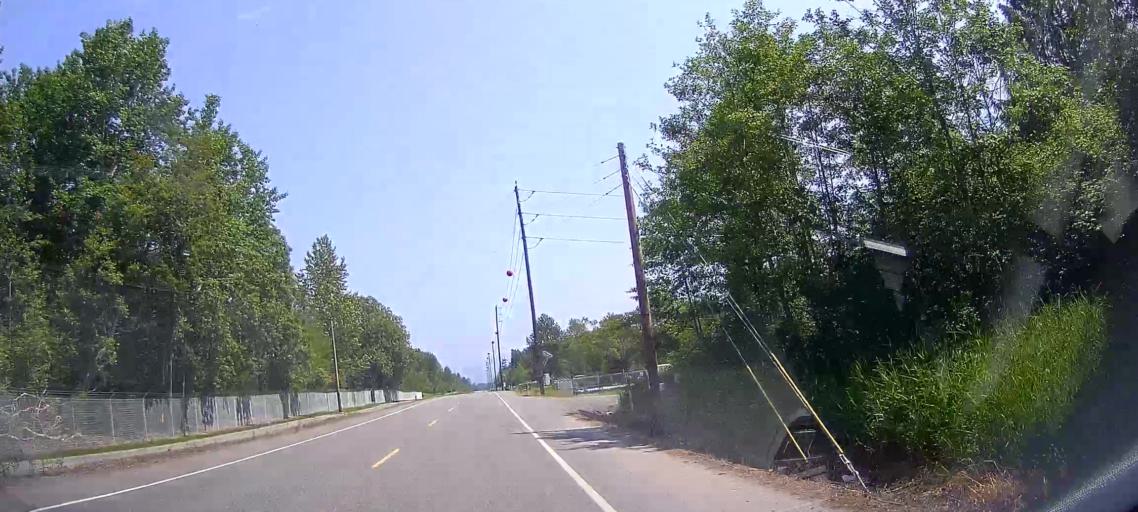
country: US
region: Washington
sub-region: Skagit County
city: Mount Vernon
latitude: 48.4576
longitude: -122.4339
